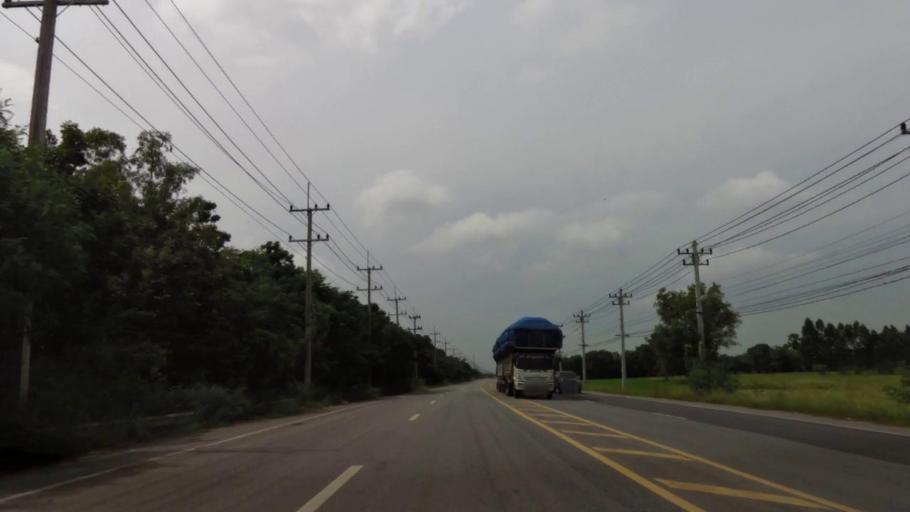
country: TH
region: Lop Buri
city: Ban Mi
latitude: 15.0631
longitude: 100.6111
